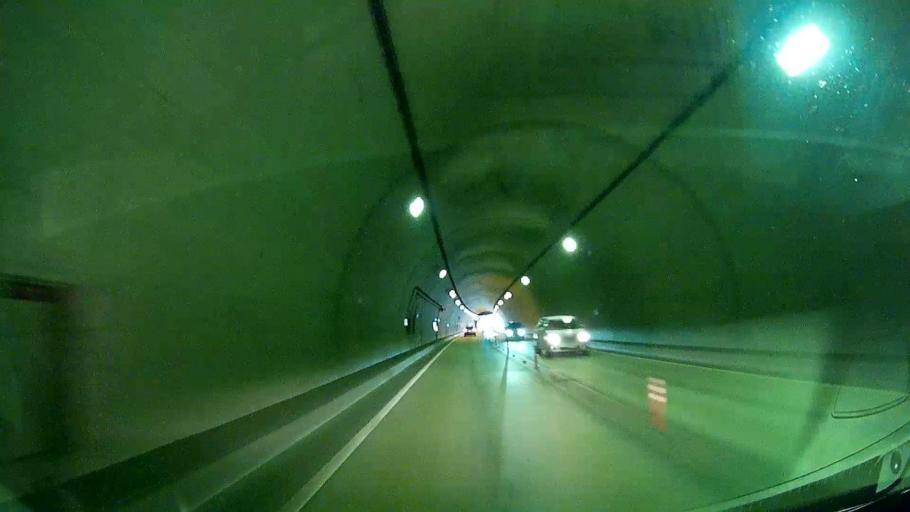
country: JP
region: Shizuoka
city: Shizuoka-shi
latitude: 35.0266
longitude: 138.3822
